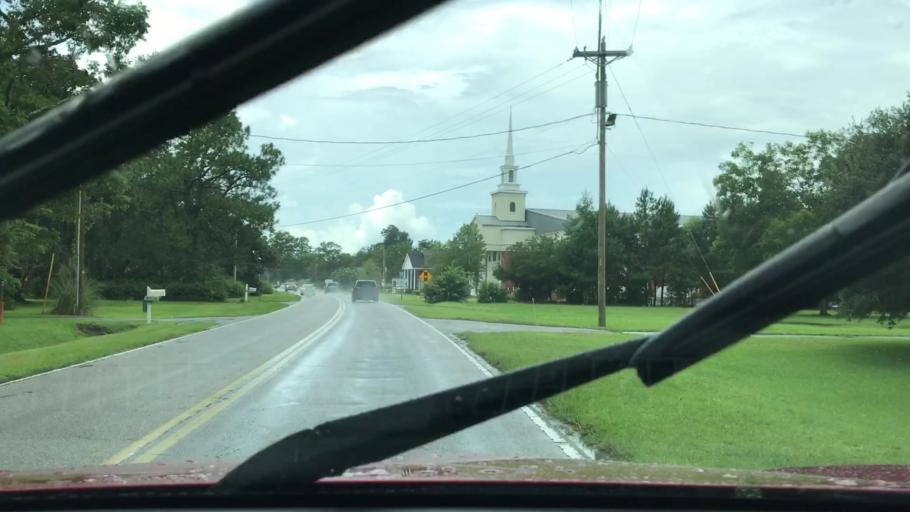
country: US
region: South Carolina
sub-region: Horry County
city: Red Hill
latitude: 33.8481
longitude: -79.0227
